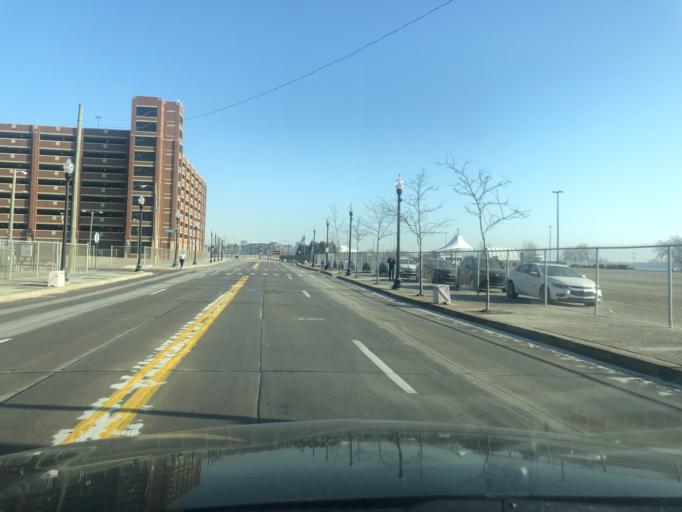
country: US
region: Michigan
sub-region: Wayne County
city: Detroit
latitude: 42.3298
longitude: -83.0352
